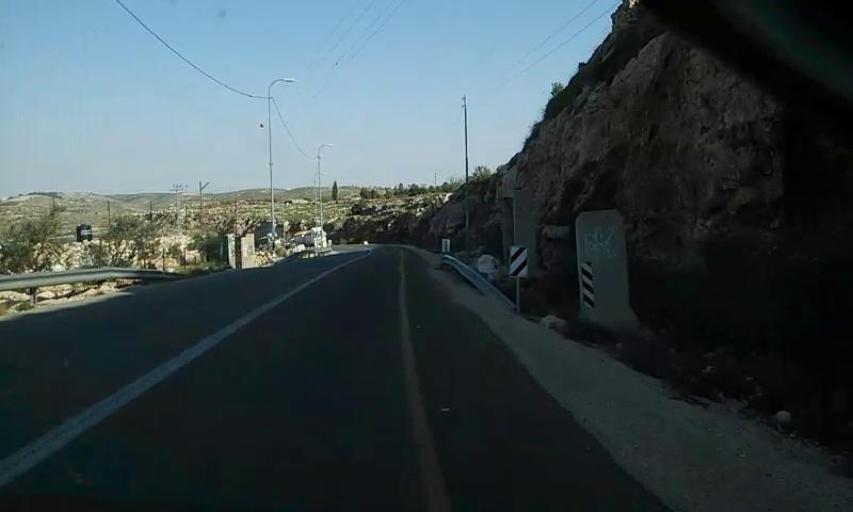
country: PS
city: Khallat ad Dar
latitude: 31.5018
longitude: 35.1116
